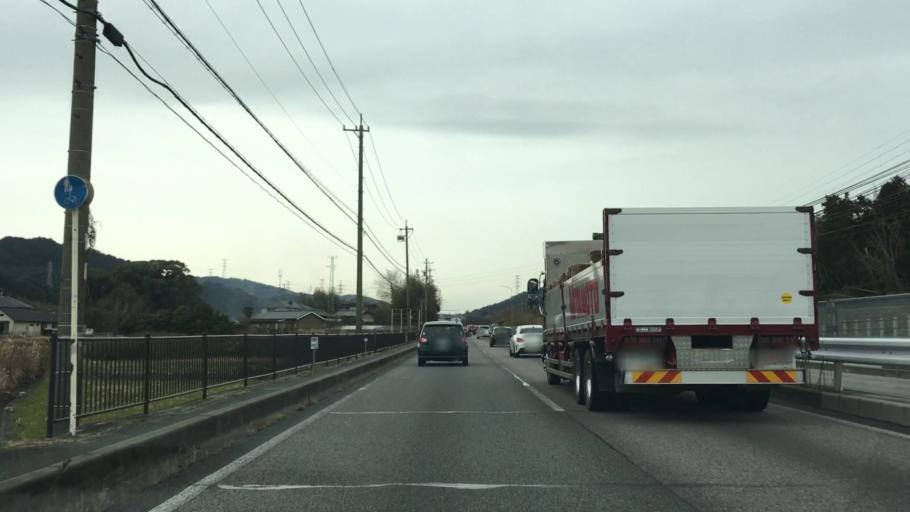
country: JP
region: Aichi
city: Gamagori
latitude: 34.8642
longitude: 137.3024
